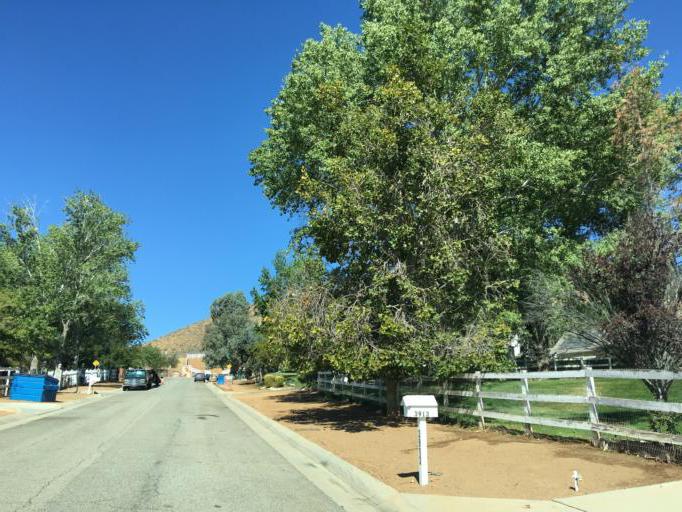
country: US
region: California
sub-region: Los Angeles County
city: Acton
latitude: 34.4976
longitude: -118.2004
